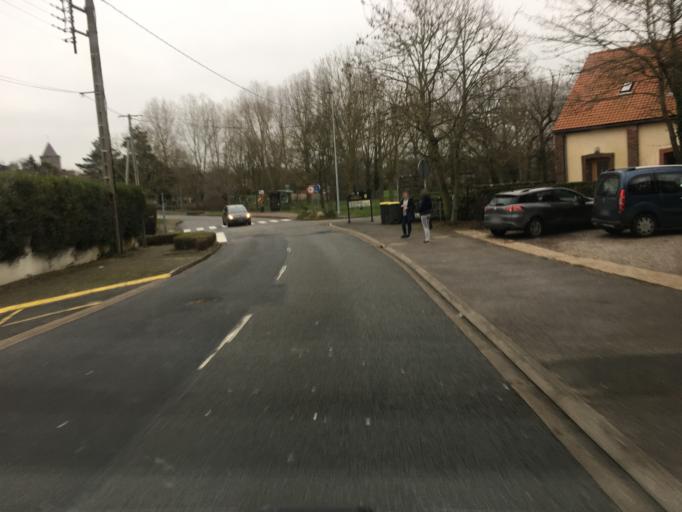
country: FR
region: Nord-Pas-de-Calais
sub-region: Departement du Pas-de-Calais
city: Wimille
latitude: 50.7643
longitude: 1.6272
